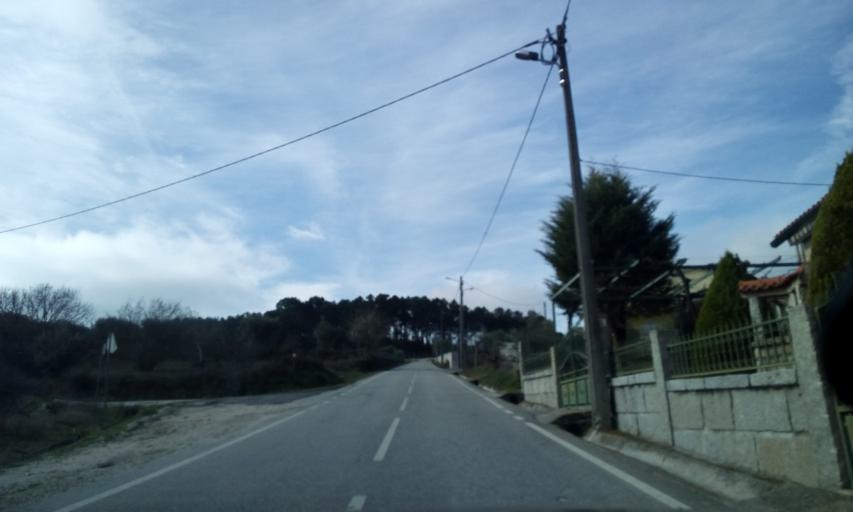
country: PT
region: Guarda
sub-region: Fornos de Algodres
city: Fornos de Algodres
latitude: 40.7014
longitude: -7.5606
